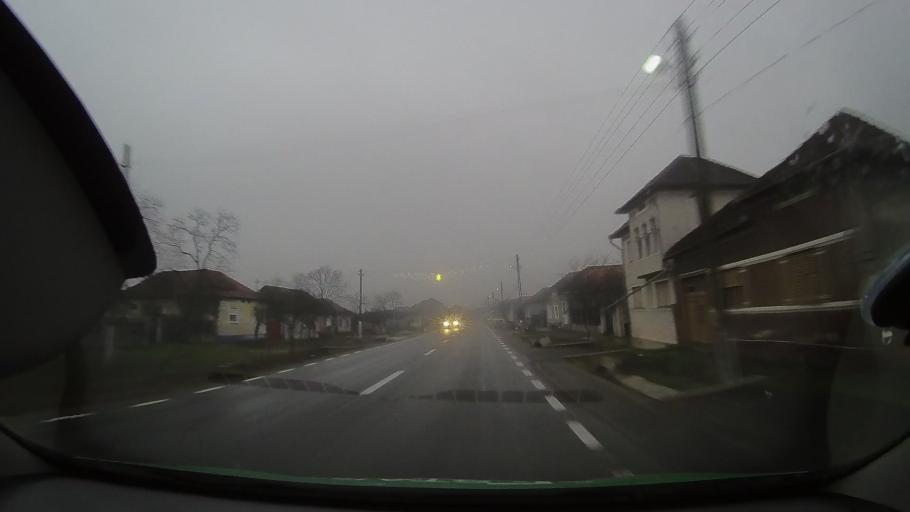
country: RO
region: Arad
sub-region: Comuna Craiova
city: Craiova
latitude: 46.6322
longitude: 21.9581
